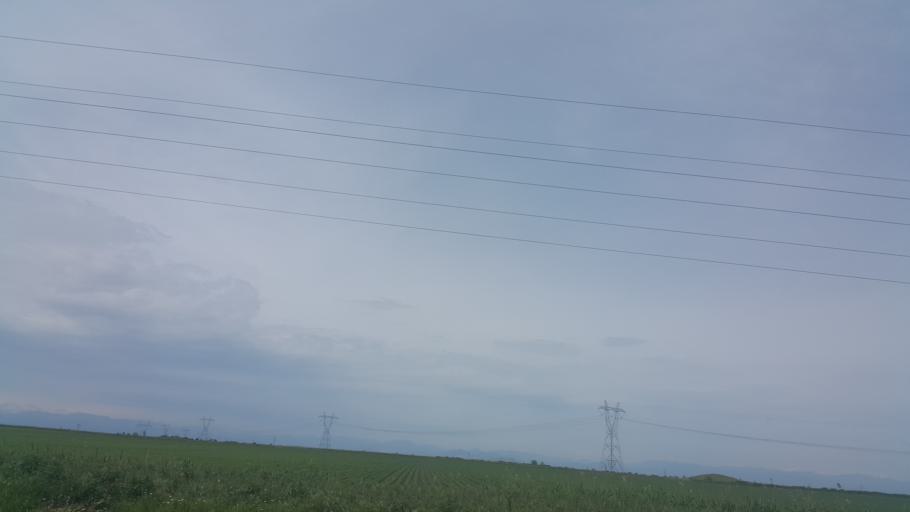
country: TR
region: Adana
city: Ceyhan
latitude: 37.0601
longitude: 35.9134
